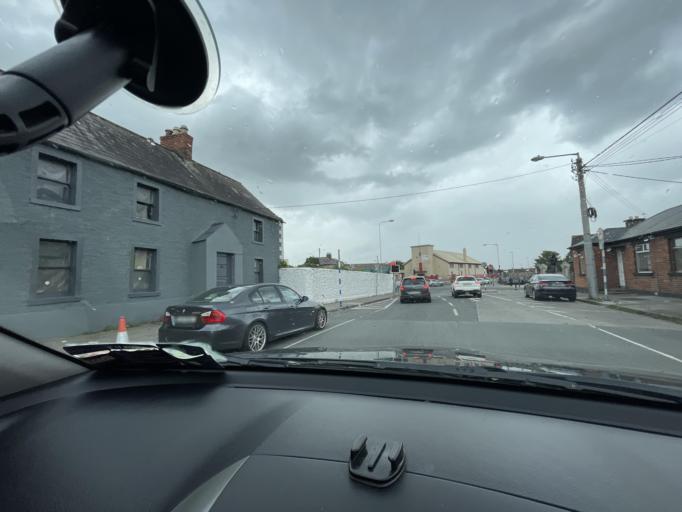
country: IE
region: Leinster
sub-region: Lu
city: Drogheda
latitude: 53.7233
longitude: -6.3562
